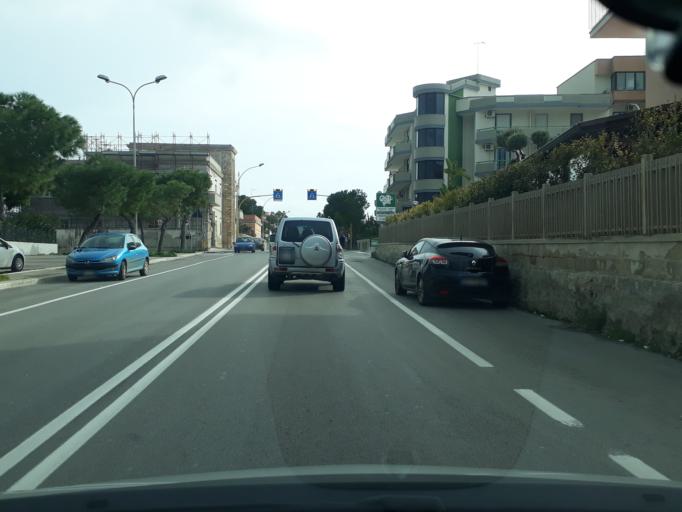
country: IT
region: Apulia
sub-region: Provincia di Bari
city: Monopoli
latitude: 40.9509
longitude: 17.2876
